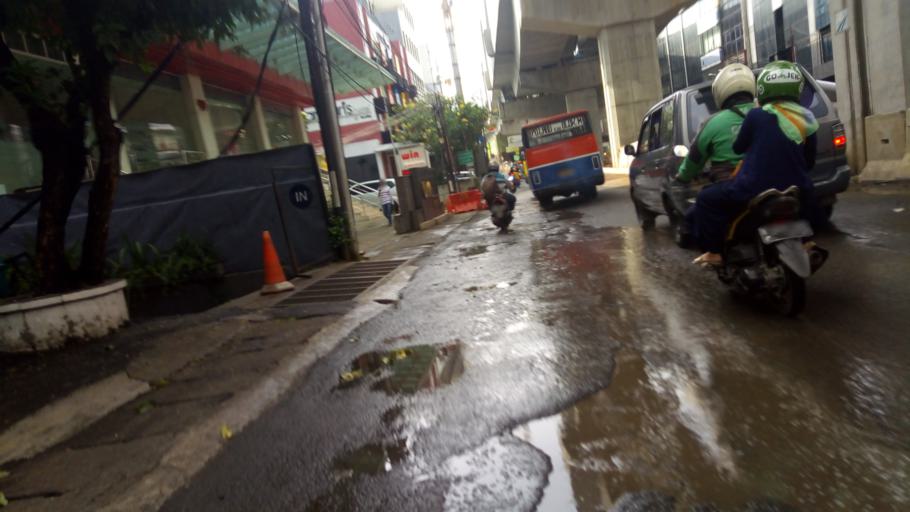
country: ID
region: Jakarta Raya
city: Jakarta
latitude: -6.2470
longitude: 106.7979
